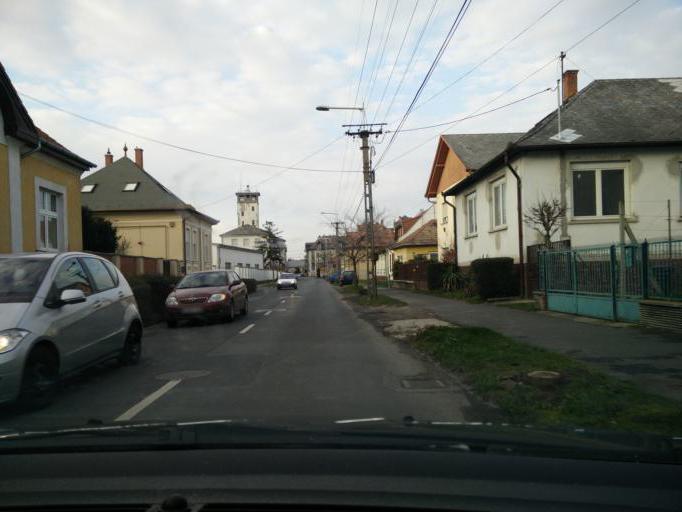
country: HU
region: Zala
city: Zalaegerszeg
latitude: 46.8438
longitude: 16.8399
